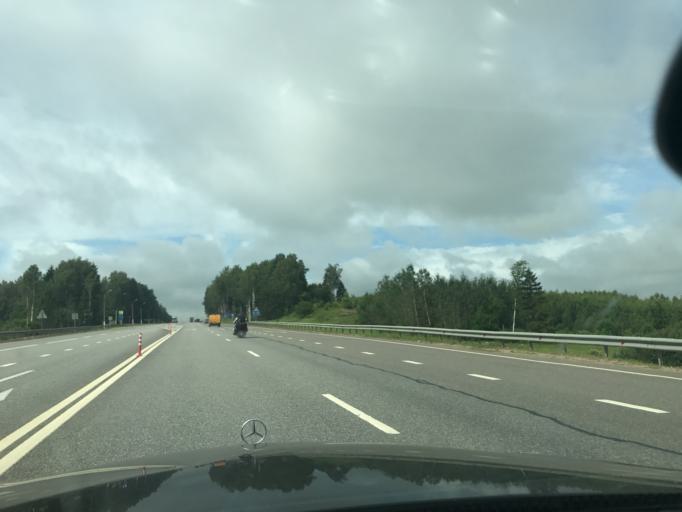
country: RU
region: Smolensk
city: Kardymovo
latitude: 55.0135
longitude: 32.2946
